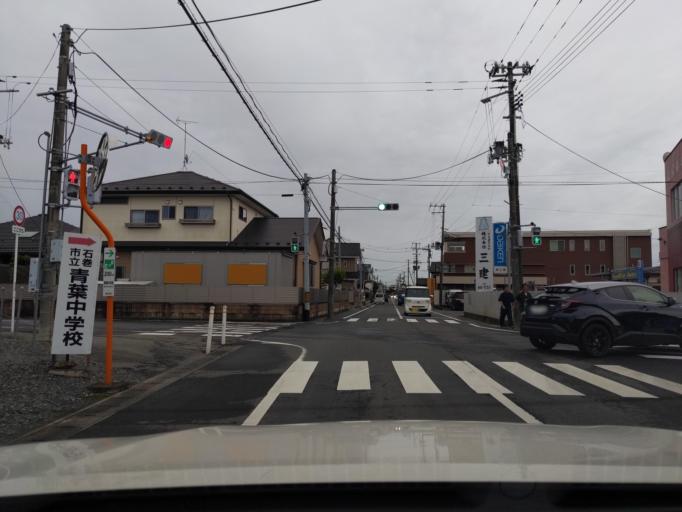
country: JP
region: Miyagi
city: Ishinomaki
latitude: 38.4341
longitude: 141.2649
